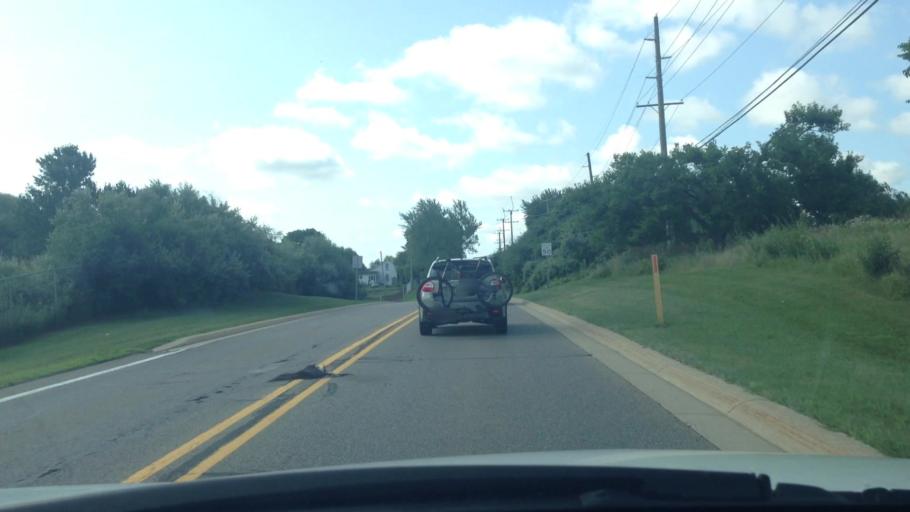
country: US
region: Michigan
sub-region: Oakland County
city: Waterford
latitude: 42.6297
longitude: -83.4426
